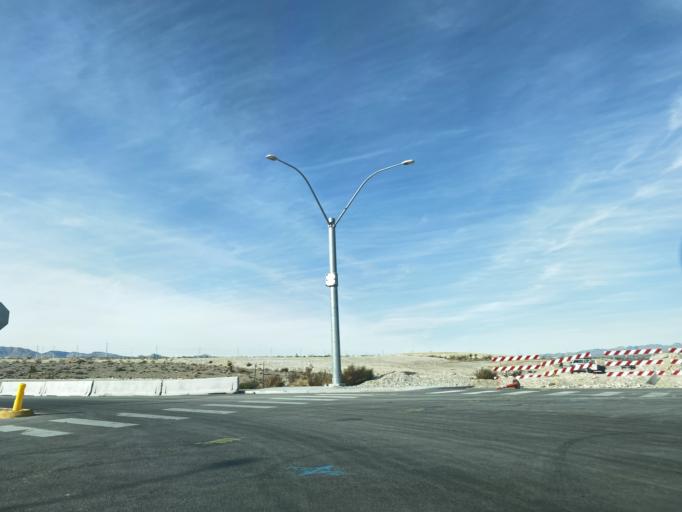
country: US
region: Nevada
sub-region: Clark County
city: Summerlin South
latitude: 36.3141
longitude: -115.3150
